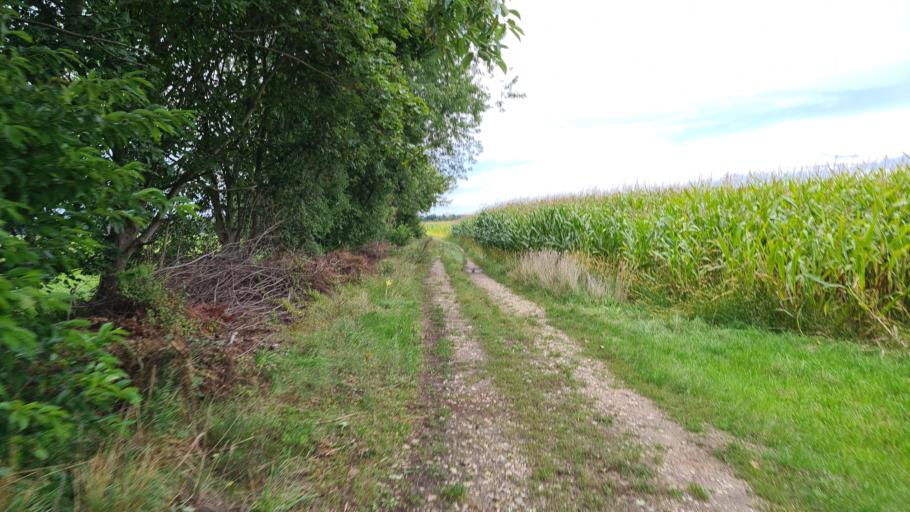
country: DE
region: Brandenburg
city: Bad Liebenwerda
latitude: 51.5281
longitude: 13.3738
